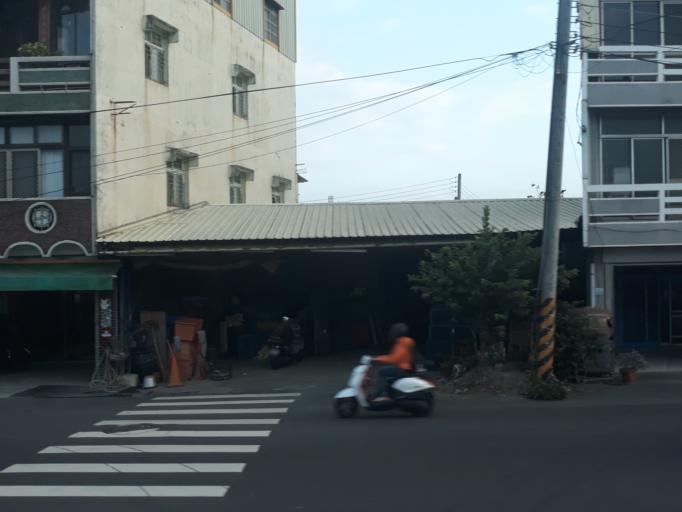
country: TW
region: Taiwan
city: Xinying
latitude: 23.1844
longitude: 120.2398
